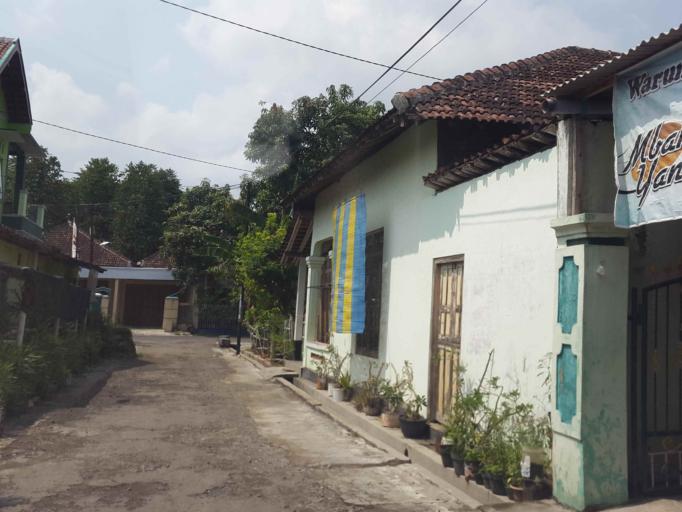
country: ID
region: Central Java
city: Jaten
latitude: -7.5920
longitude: 110.9420
